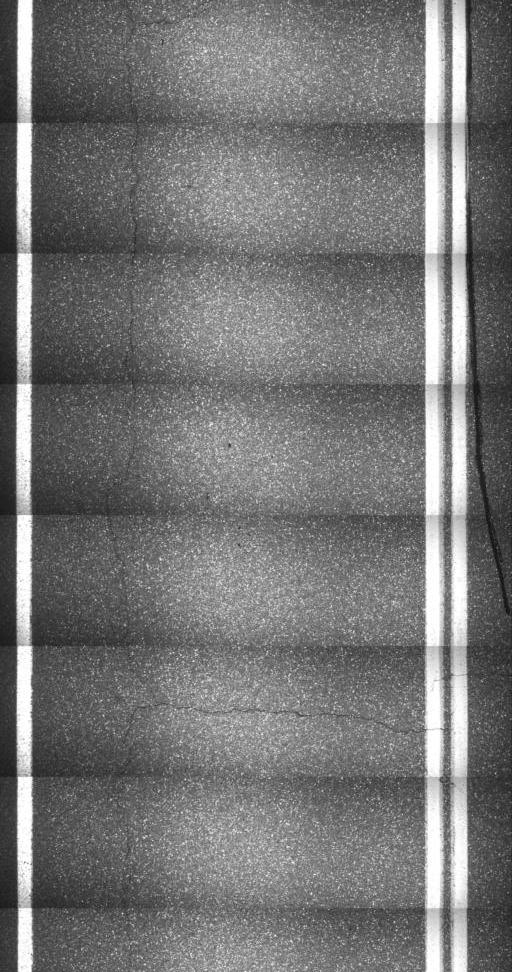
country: US
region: Vermont
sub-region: Orange County
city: Chelsea
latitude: 44.1090
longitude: -72.3185
